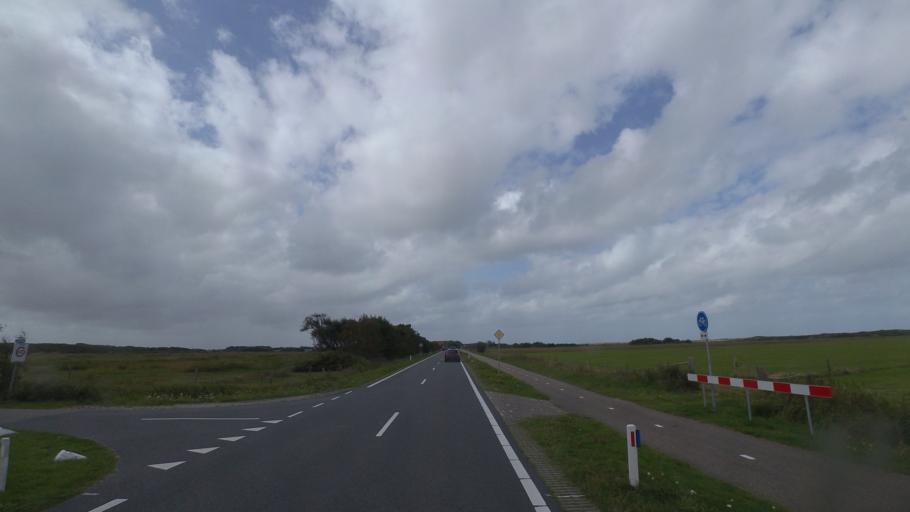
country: NL
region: Friesland
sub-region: Gemeente Ameland
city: Hollum
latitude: 53.4465
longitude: 5.6758
